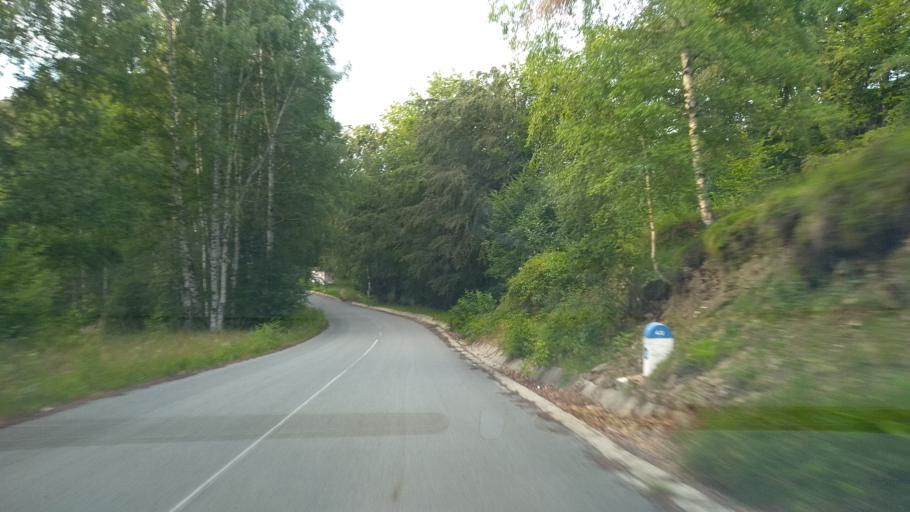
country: RO
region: Hunedoara
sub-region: Municipiul  Vulcan
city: Jiu-Paroseni
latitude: 45.3401
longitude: 23.2914
